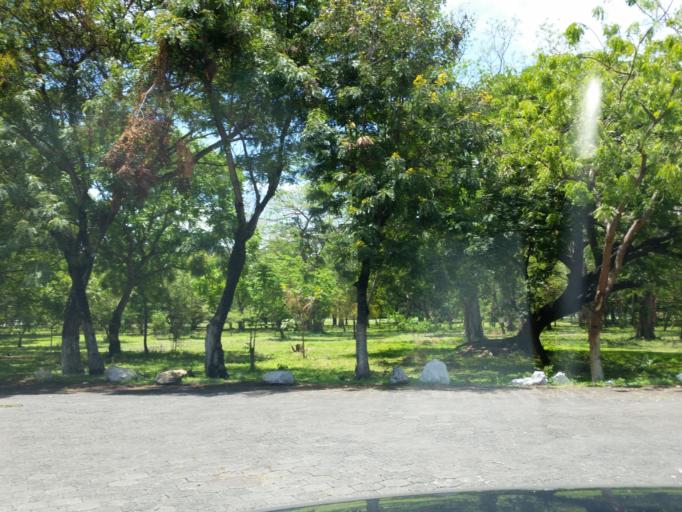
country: NI
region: Granada
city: Granada
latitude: 11.9213
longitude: -85.9420
